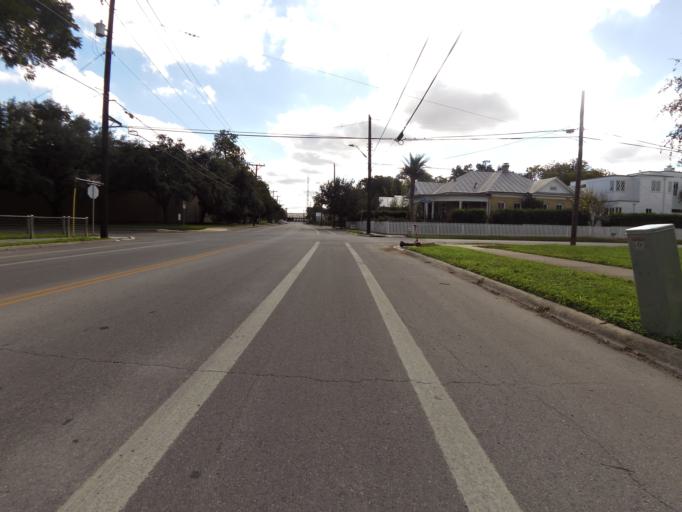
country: US
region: Texas
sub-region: Bexar County
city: San Antonio
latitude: 29.4133
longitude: -98.4975
